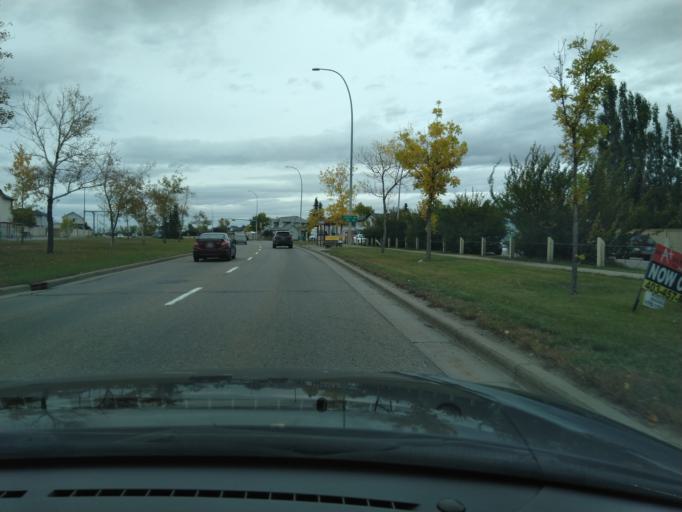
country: CA
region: Alberta
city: Calgary
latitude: 51.1459
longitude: -114.0647
